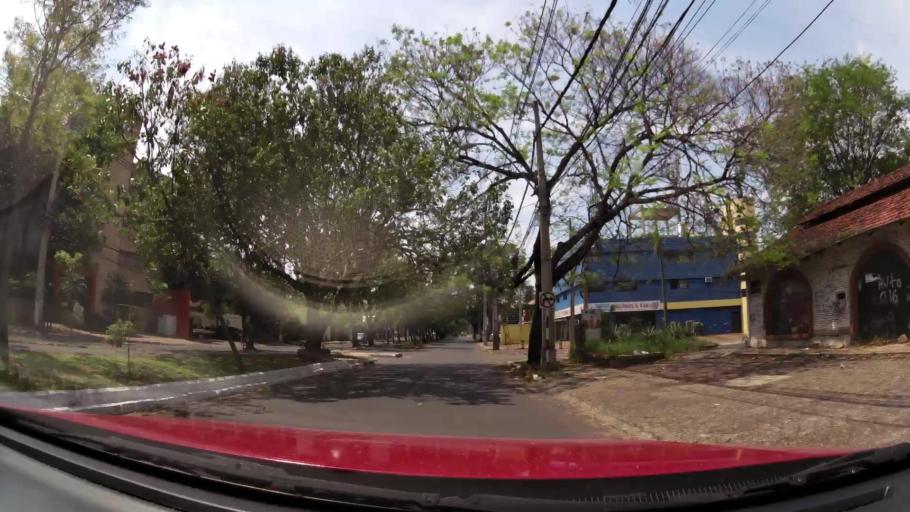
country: PY
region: Central
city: Lambare
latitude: -25.2993
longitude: -57.5723
